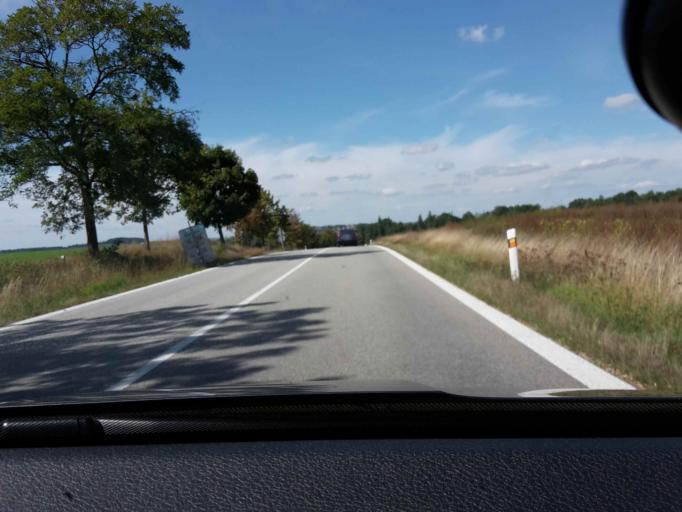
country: CZ
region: Jihocesky
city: Kardasova Recice
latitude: 49.1763
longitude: 14.8687
